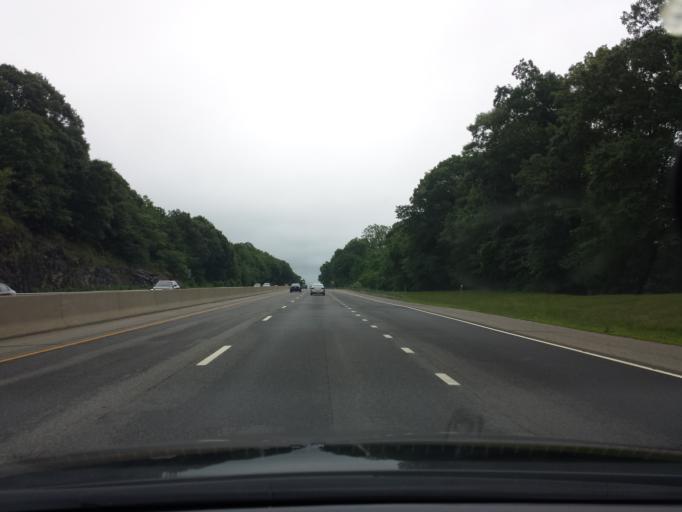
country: US
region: Connecticut
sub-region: Middlesex County
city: Westbrook Center
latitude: 41.2915
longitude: -72.4406
